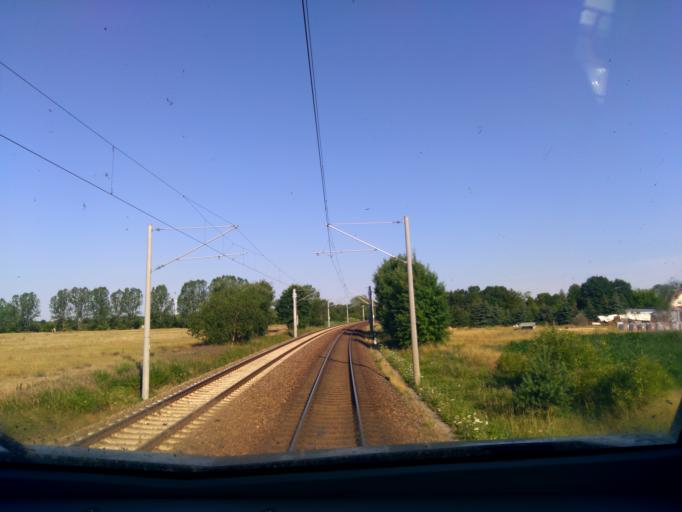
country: DE
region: Brandenburg
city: Luebben
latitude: 51.9567
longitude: 13.8327
